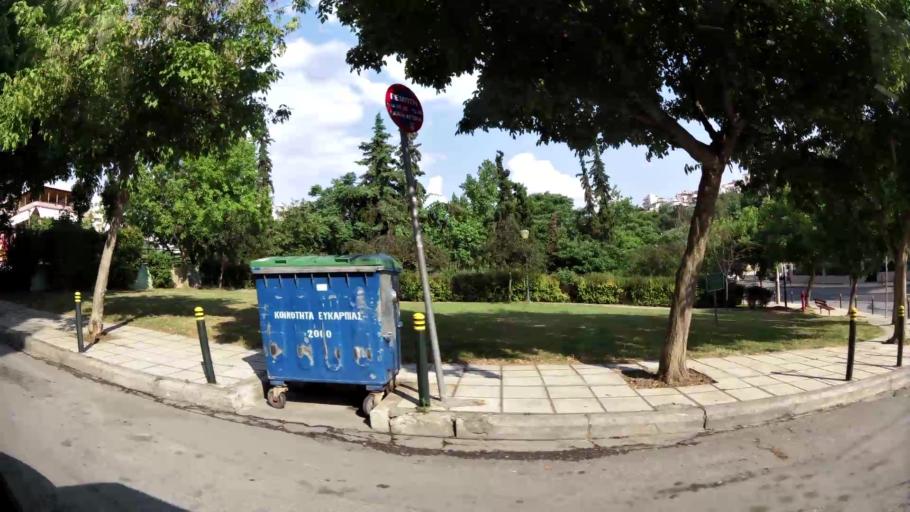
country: GR
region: Central Macedonia
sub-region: Nomos Thessalonikis
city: Polichni
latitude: 40.6597
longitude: 22.9499
